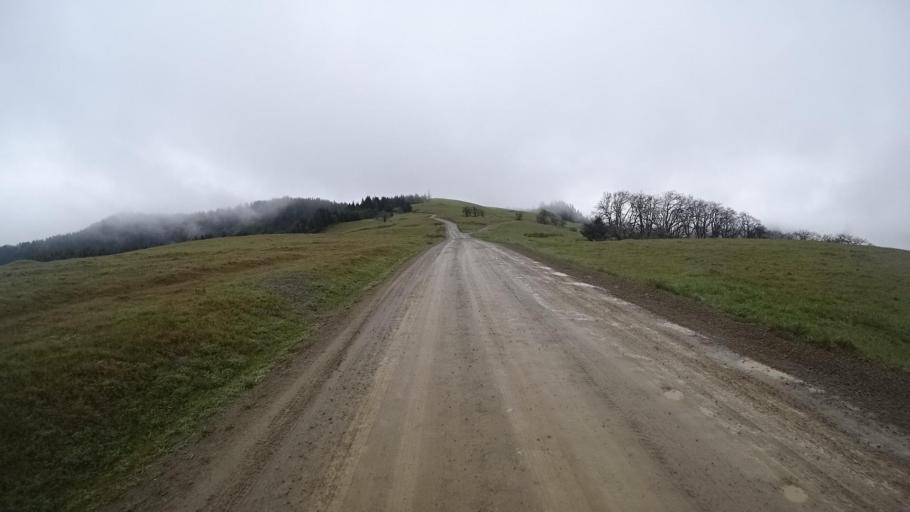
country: US
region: California
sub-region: Humboldt County
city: Westhaven-Moonstone
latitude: 41.1442
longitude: -123.8671
